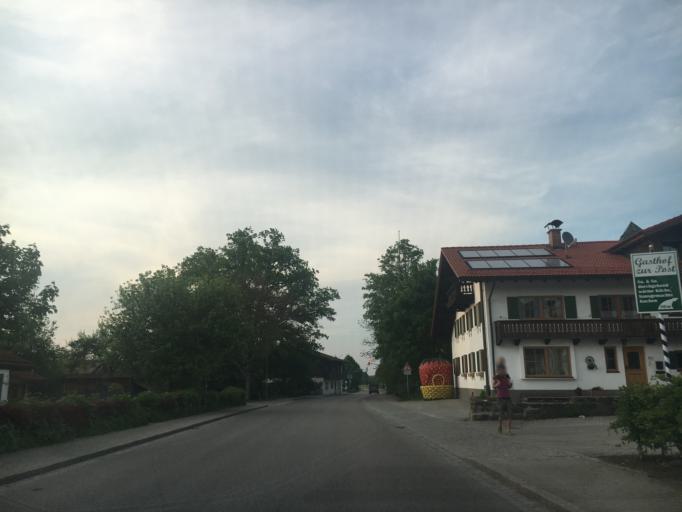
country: DE
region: Bavaria
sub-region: Upper Bavaria
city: Benediktbeuern
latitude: 47.7068
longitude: 11.4114
